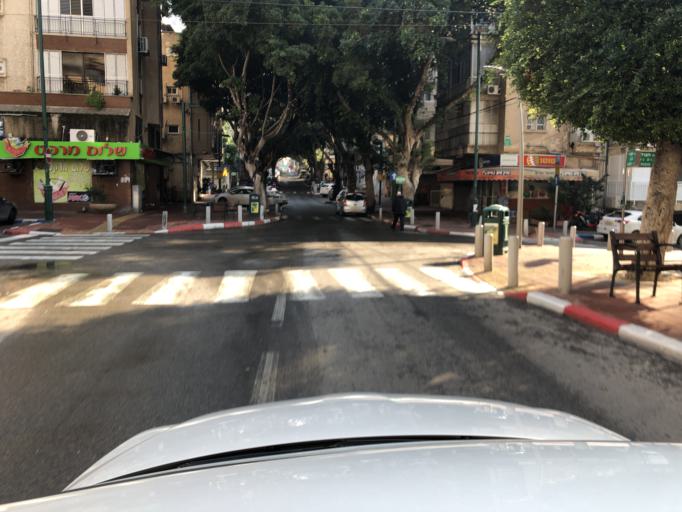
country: IL
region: Tel Aviv
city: Ramat Gan
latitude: 32.0921
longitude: 34.8181
